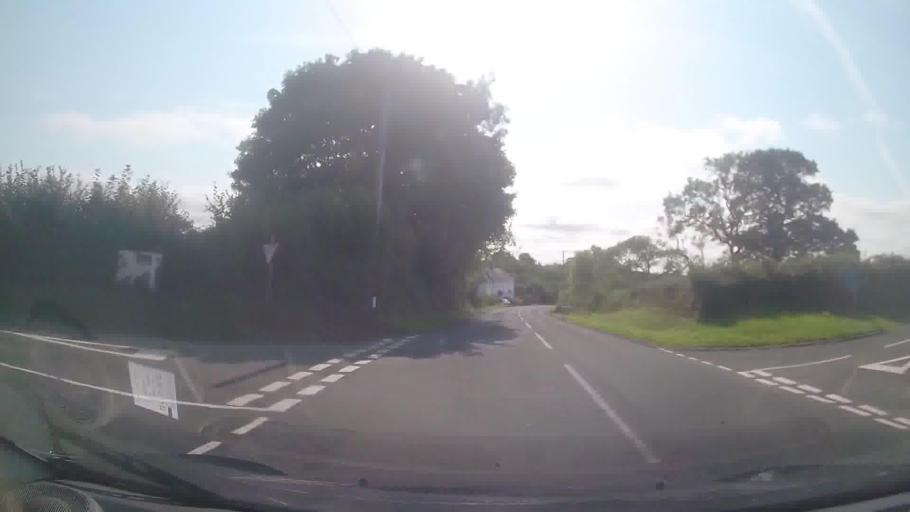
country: GB
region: Wales
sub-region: Pembrokeshire
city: Saundersfoot
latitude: 51.7401
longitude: -4.6800
